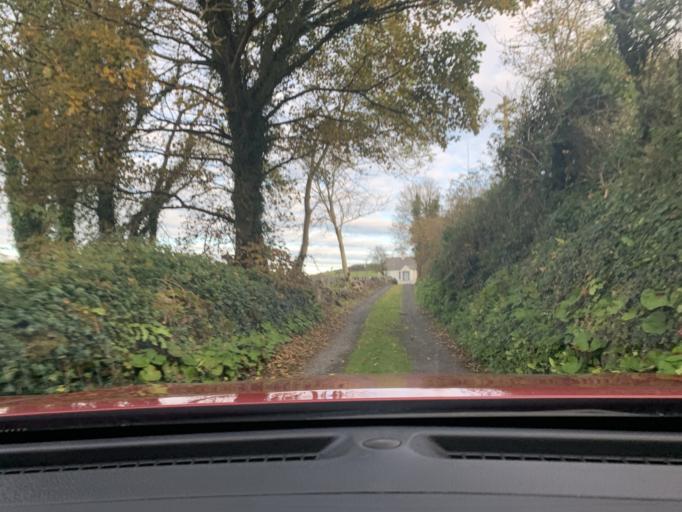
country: IE
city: Ballisodare
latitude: 54.2329
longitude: -8.5033
